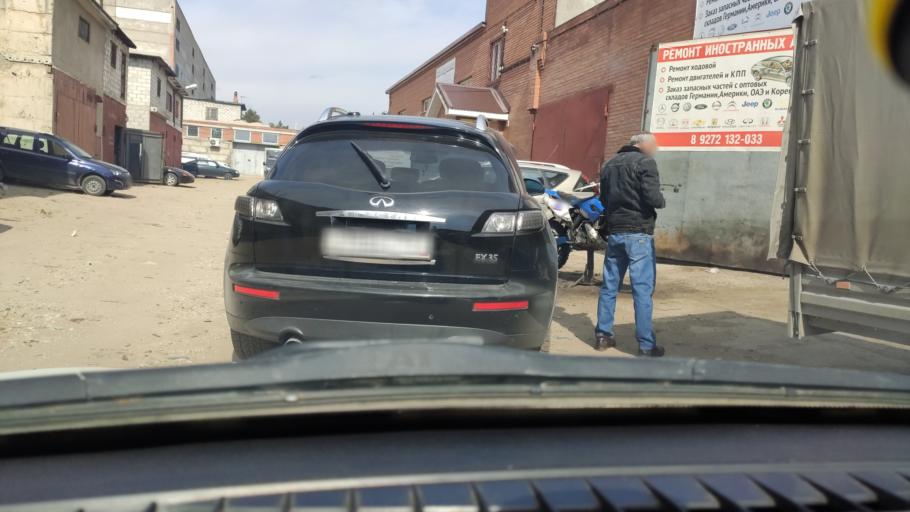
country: RU
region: Samara
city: Zhigulevsk
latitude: 53.4907
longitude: 49.4822
